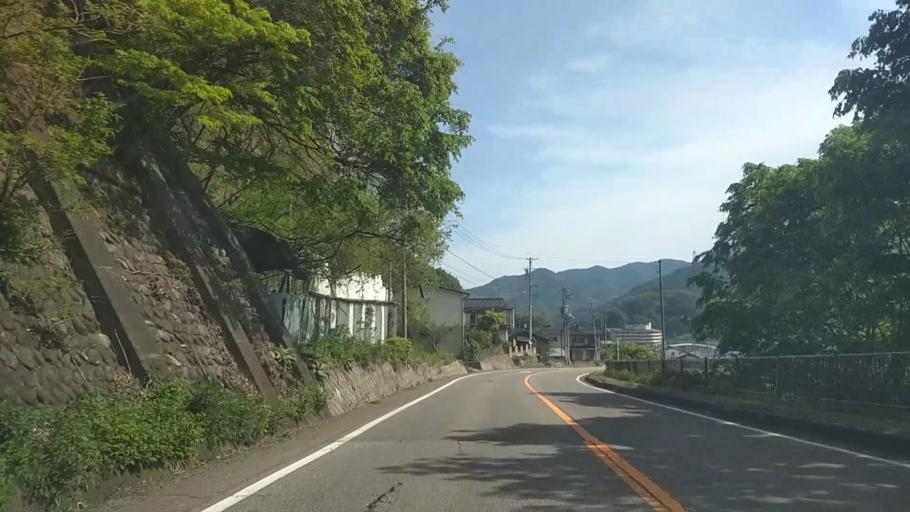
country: JP
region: Nagano
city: Saku
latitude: 36.0867
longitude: 138.4800
